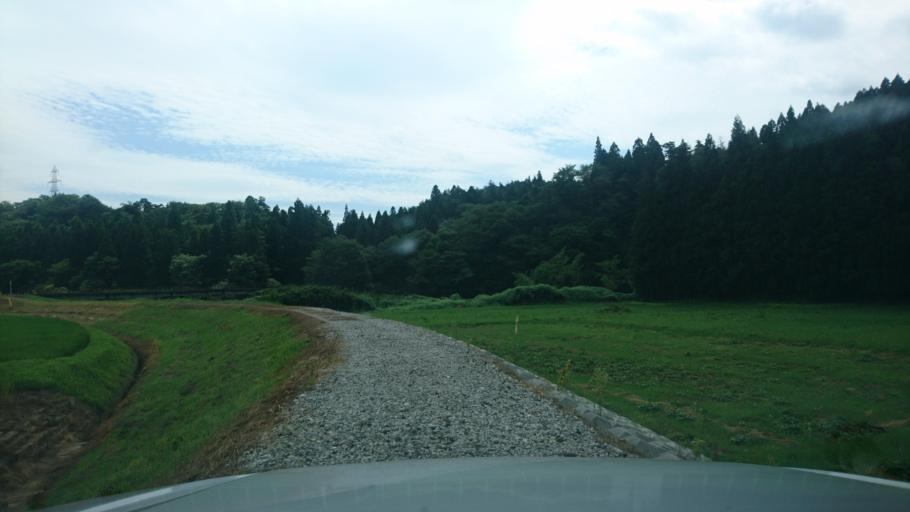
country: JP
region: Iwate
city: Ichinoseki
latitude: 38.8038
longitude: 140.9492
